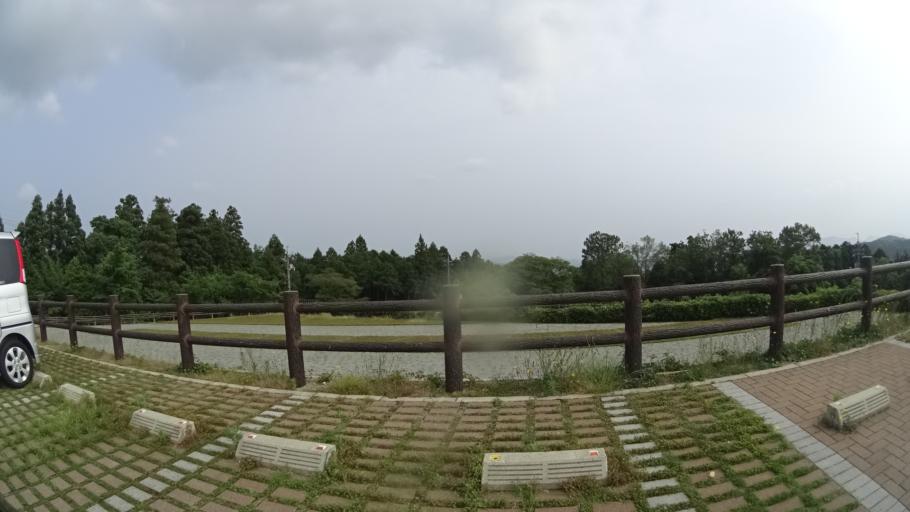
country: JP
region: Yamaguchi
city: Ogori-shimogo
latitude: 34.2342
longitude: 131.3047
